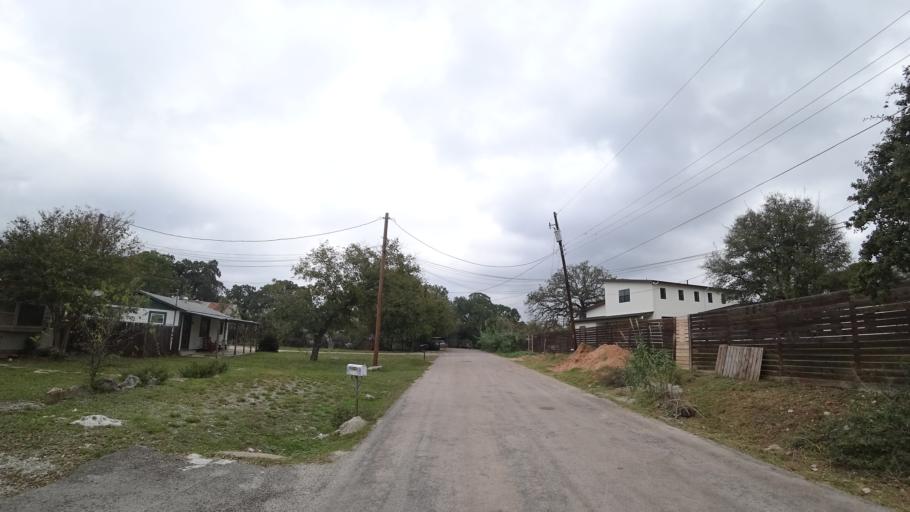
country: US
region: Texas
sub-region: Travis County
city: Bee Cave
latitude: 30.3331
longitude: -97.9254
